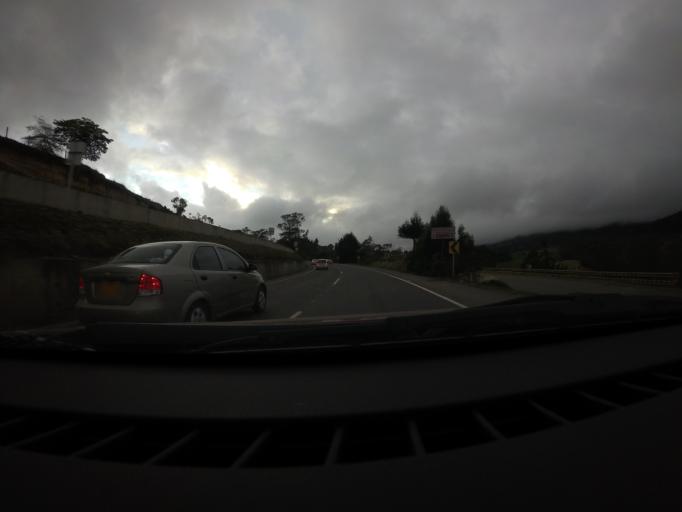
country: CO
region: Boyaca
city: Samaca
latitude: 5.4373
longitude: -73.4470
